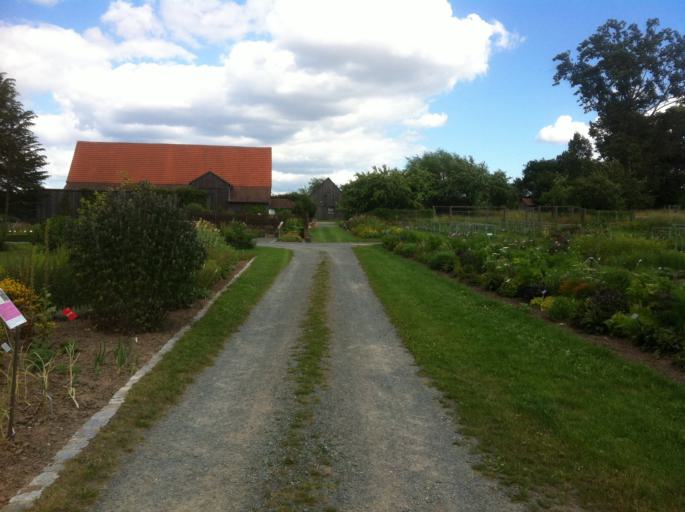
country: DE
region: Bavaria
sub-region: Upper Franconia
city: Bayreuth
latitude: 49.9221
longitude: 11.5873
